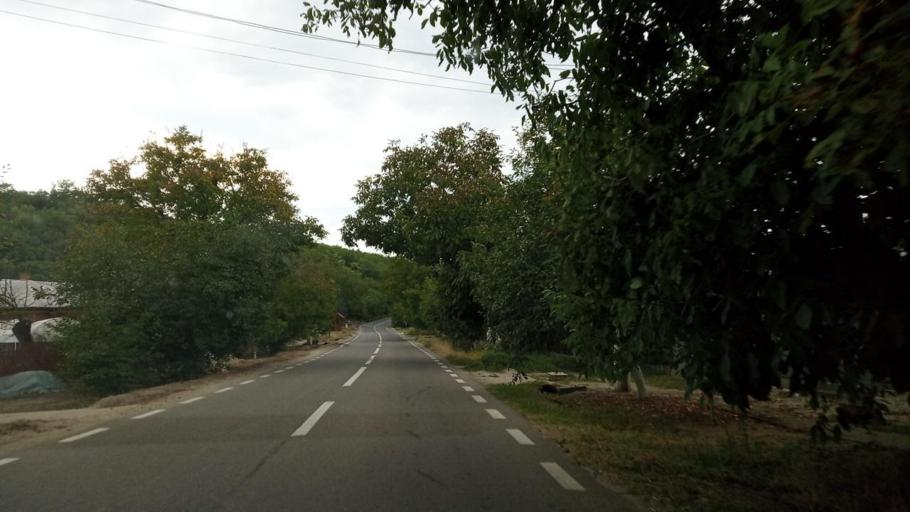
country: RO
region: Giurgiu
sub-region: Comuna Izvoarele
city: Isvoarele
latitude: 44.1695
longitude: 26.2936
